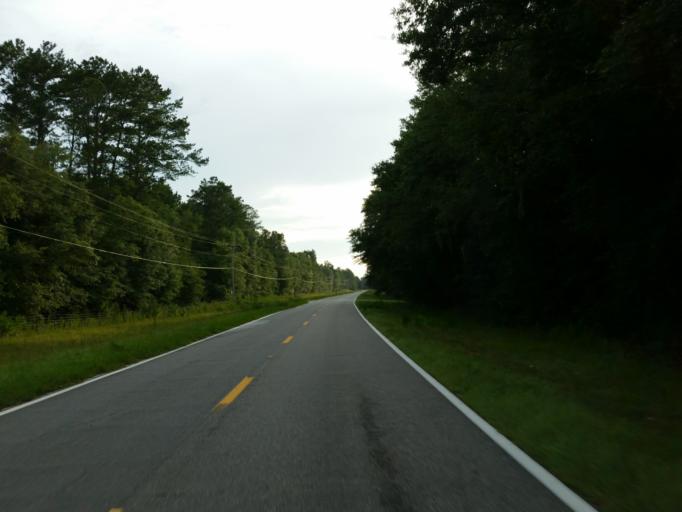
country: US
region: Florida
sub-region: Alachua County
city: High Springs
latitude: 29.9529
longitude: -82.5753
